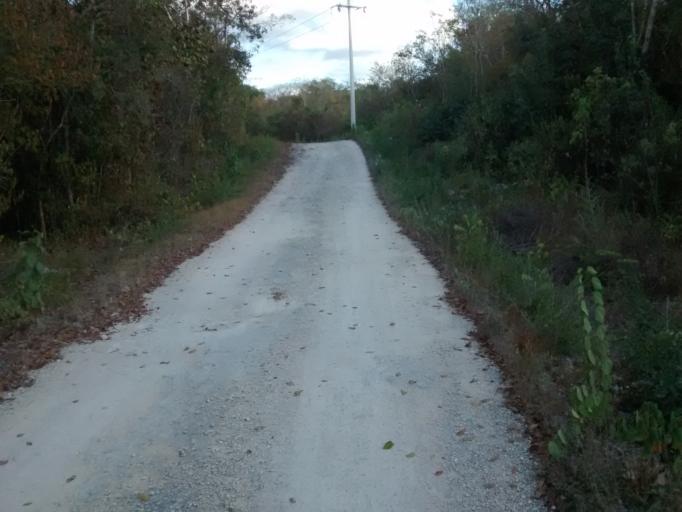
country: MX
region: Yucatan
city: Chichimila
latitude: 20.4477
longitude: -88.2002
